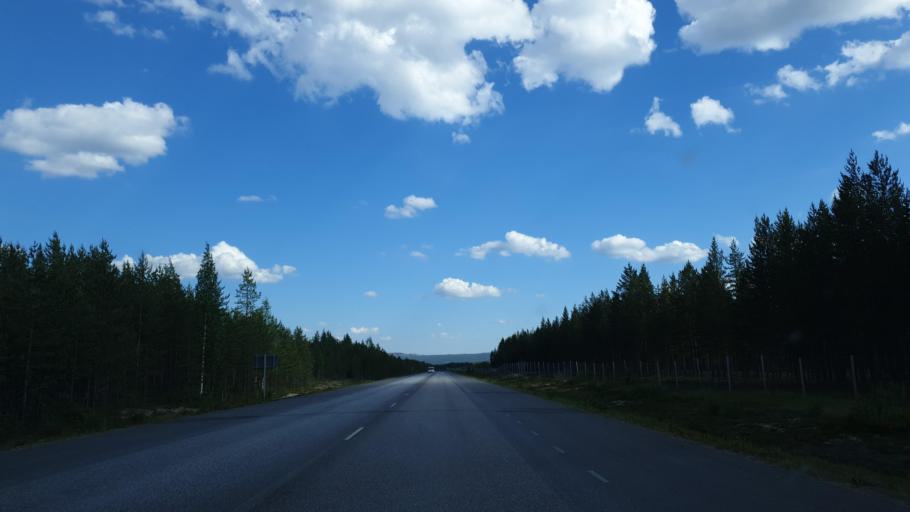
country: SE
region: Norrbotten
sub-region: Alvsbyns Kommun
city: AElvsbyn
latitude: 65.8254
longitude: 20.5582
